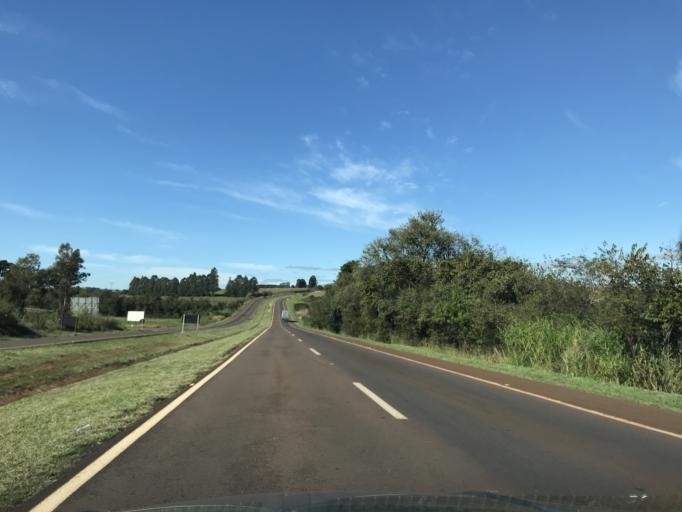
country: BR
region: Parana
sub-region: Cascavel
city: Cascavel
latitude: -24.9003
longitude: -53.5265
